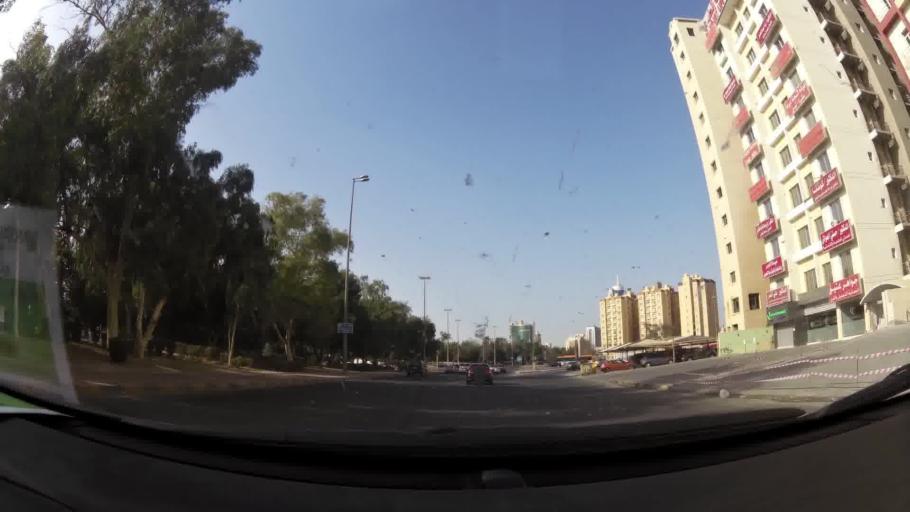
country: KW
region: Muhafazat Hawalli
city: As Salimiyah
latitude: 29.3346
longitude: 48.0729
